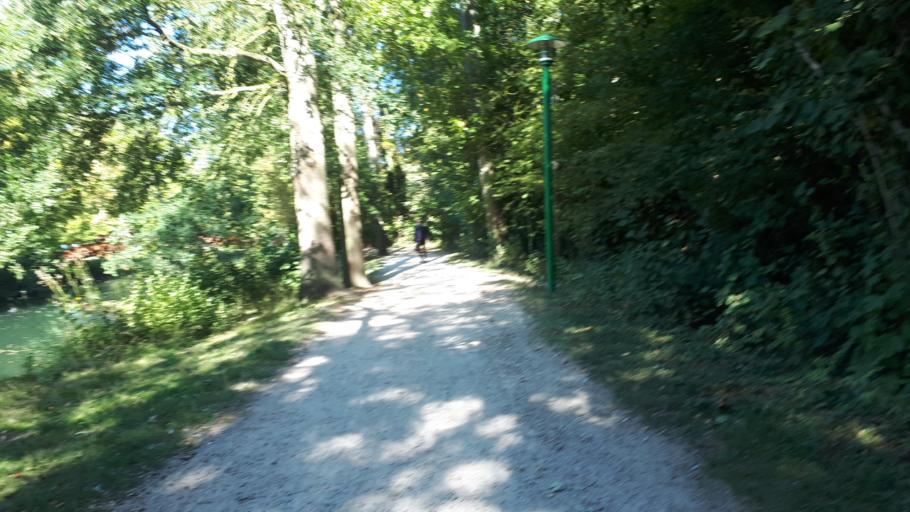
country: FR
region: Centre
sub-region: Departement d'Eure-et-Loir
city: Chartres
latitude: 48.4388
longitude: 1.5006
